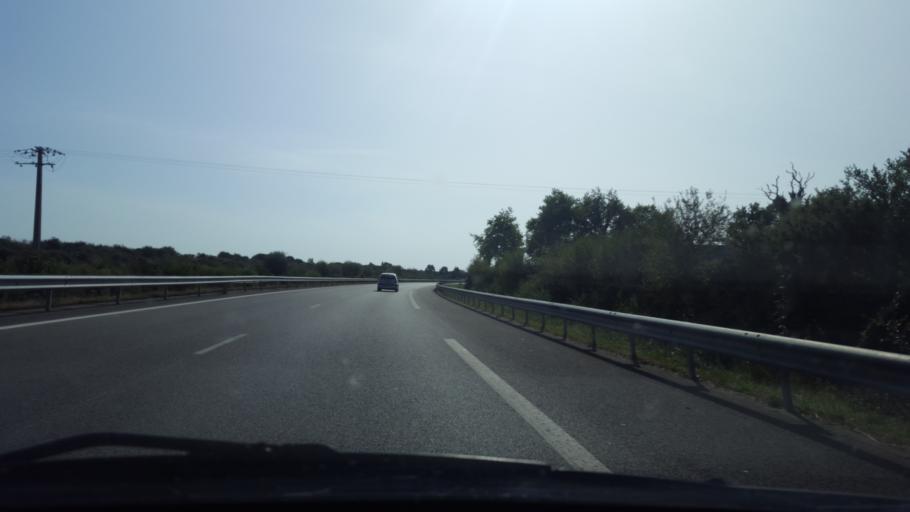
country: FR
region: Pays de la Loire
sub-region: Departement de la Loire-Atlantique
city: Saint-Philbert-de-Grand-Lieu
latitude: 47.0538
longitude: -1.6235
